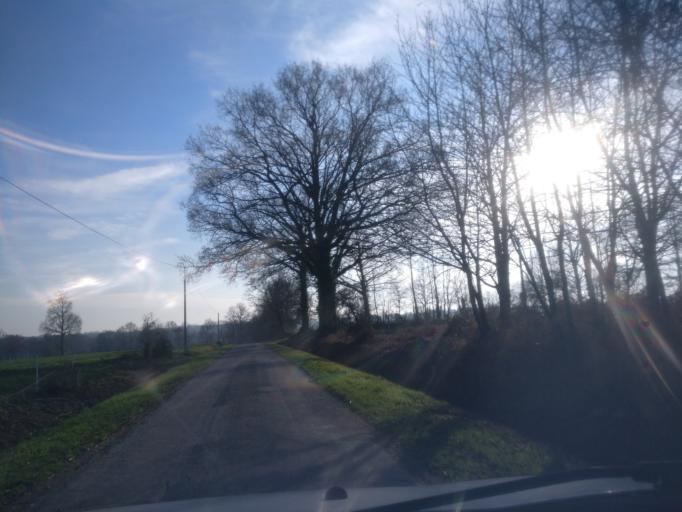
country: FR
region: Brittany
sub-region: Departement d'Ille-et-Vilaine
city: Livre-sur-Changeon
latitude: 48.2095
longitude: -1.2952
